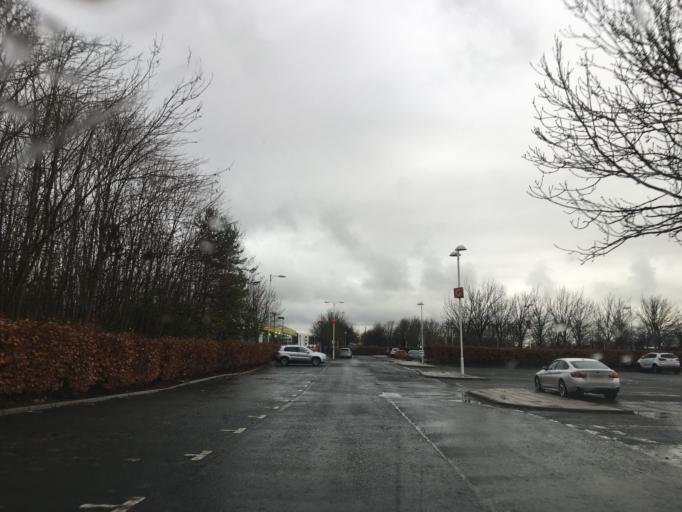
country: GB
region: Scotland
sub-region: Edinburgh
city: Currie
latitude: 55.9364
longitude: -3.3122
